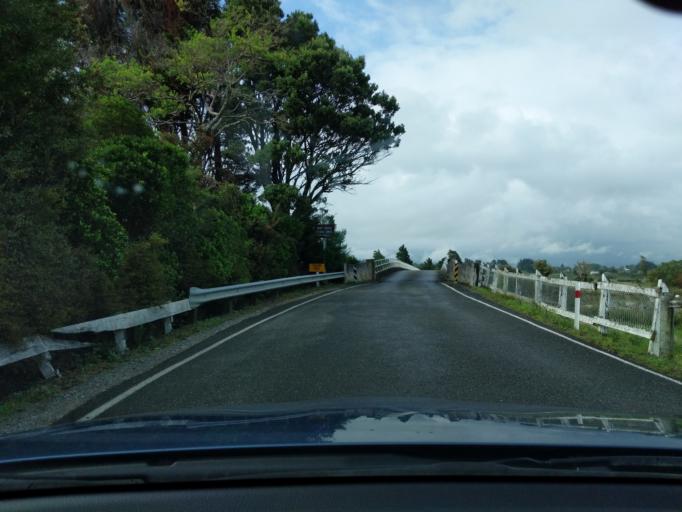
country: NZ
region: Tasman
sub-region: Tasman District
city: Takaka
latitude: -40.6741
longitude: 172.6612
